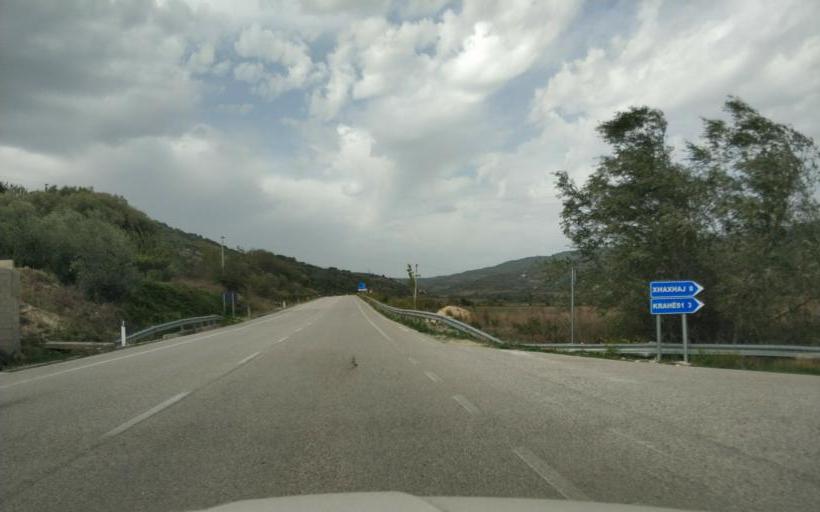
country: AL
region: Gjirokaster
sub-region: Rrethi i Tepelenes
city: Krahes
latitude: 40.4510
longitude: 19.8485
